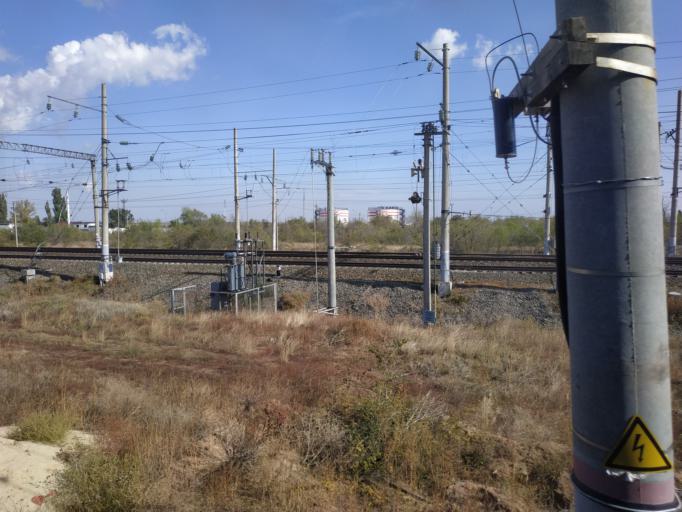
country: RU
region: Volgograd
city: Gumrak
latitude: 48.7933
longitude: 44.3645
